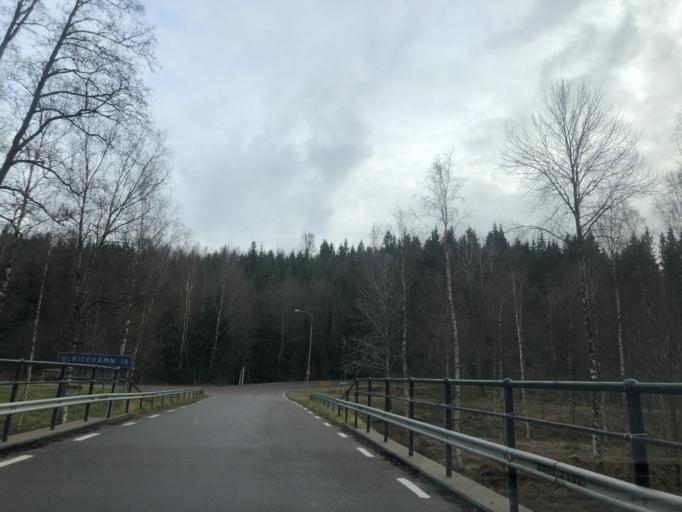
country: SE
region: Vaestra Goetaland
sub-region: Boras Kommun
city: Dalsjofors
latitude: 57.8266
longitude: 13.1934
